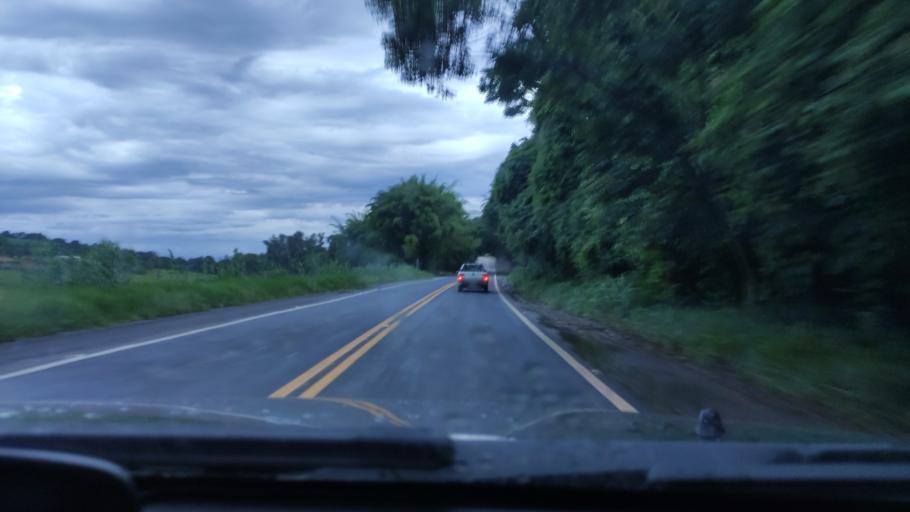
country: BR
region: Sao Paulo
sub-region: Socorro
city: Socorro
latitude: -22.6503
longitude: -46.5416
